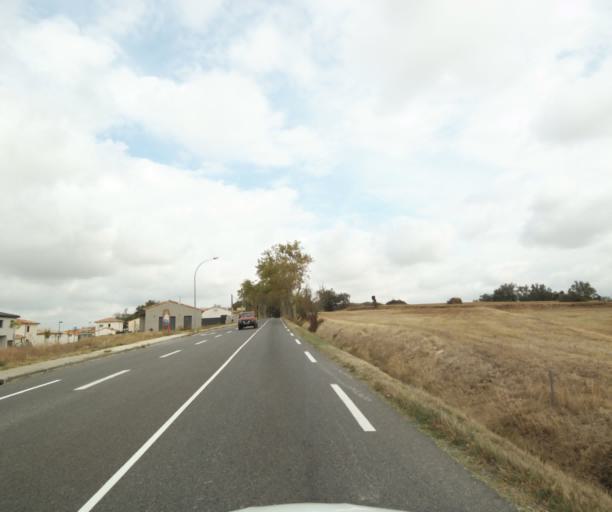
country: FR
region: Midi-Pyrenees
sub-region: Departement de la Haute-Garonne
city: Villefranche-de-Lauragais
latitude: 43.4112
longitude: 1.7163
